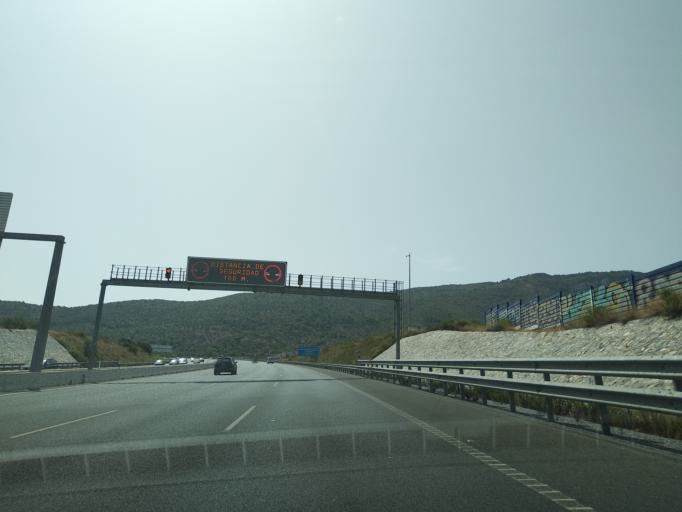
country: ES
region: Andalusia
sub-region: Provincia de Malaga
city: Alhaurin de la Torre
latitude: 36.6663
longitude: -4.5294
